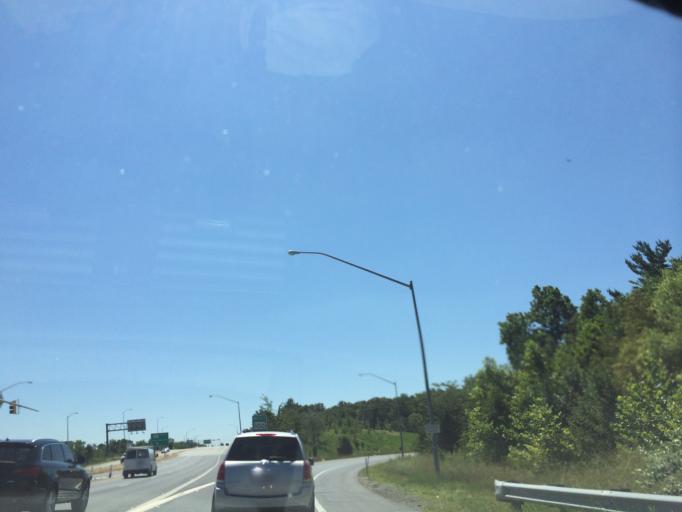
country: US
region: Maryland
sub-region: Howard County
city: Hanover
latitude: 39.1904
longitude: -76.7546
